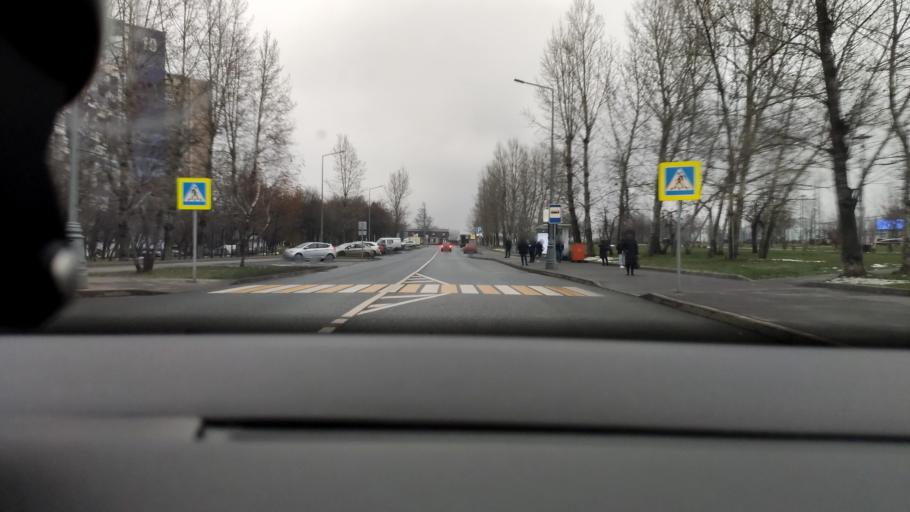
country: RU
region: Moskovskaya
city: Alekseyevka
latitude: 55.6310
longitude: 37.8015
